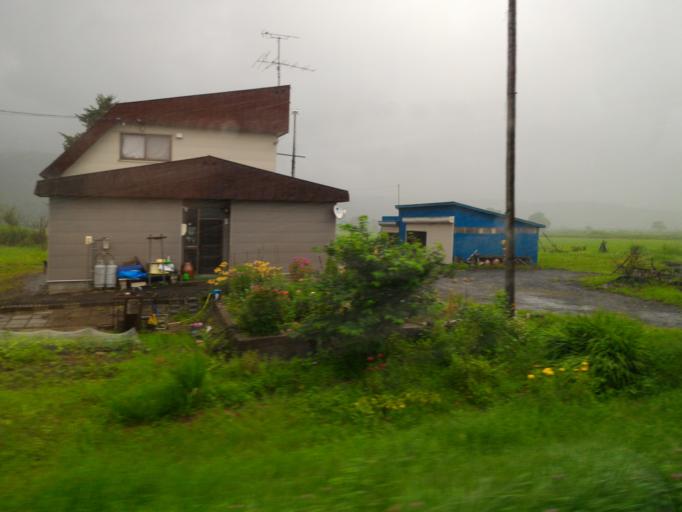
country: JP
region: Hokkaido
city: Makubetsu
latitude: 44.8577
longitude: 142.0547
